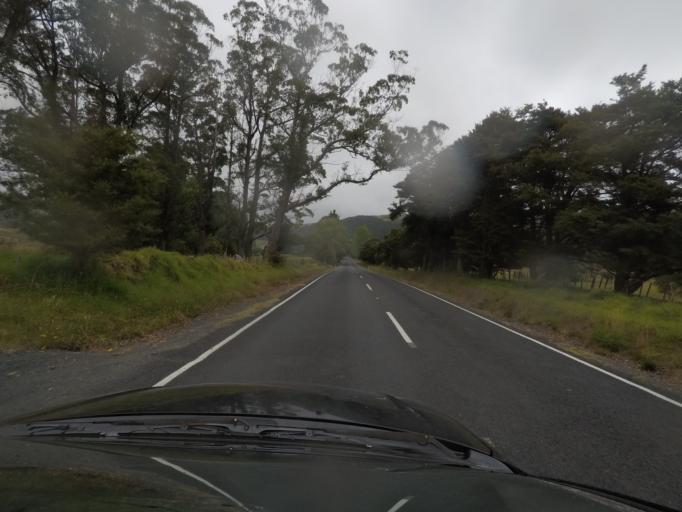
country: NZ
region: Auckland
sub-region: Auckland
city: Warkworth
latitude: -36.2636
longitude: 174.7035
